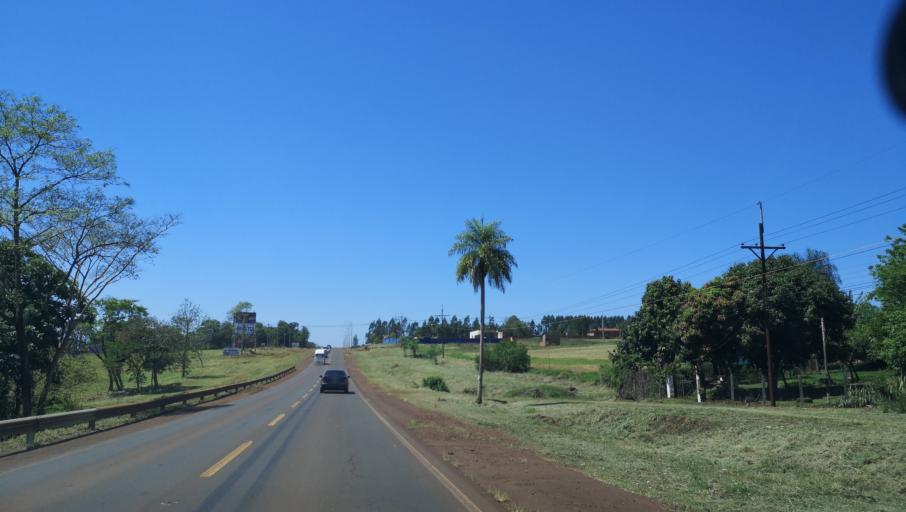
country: PY
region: Itapua
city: San Juan del Parana
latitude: -27.2715
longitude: -55.9544
